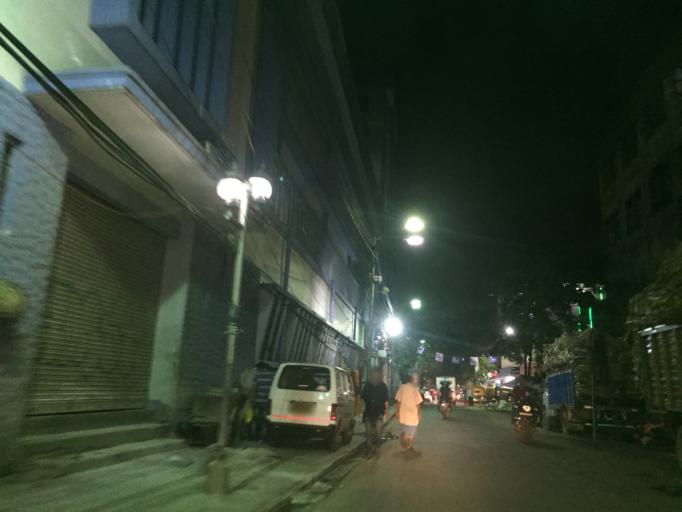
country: IN
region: West Bengal
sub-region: Kolkata
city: Bara Bazar
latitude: 22.5597
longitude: 88.3548
